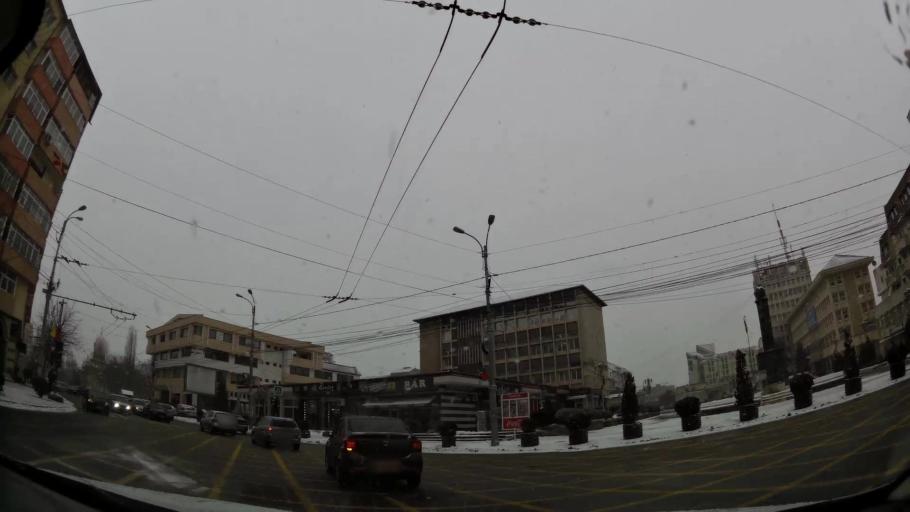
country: RO
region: Dambovita
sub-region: Municipiul Targoviste
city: Targoviste
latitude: 44.9264
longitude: 25.4631
